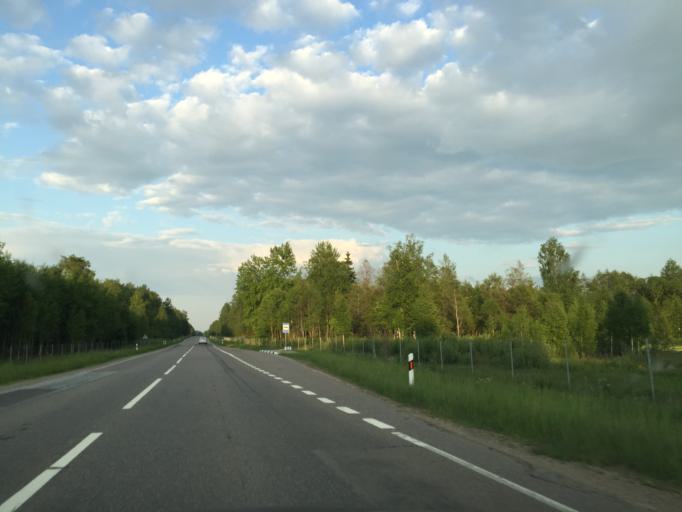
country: LT
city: Kursenai
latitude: 56.0034
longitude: 22.7572
